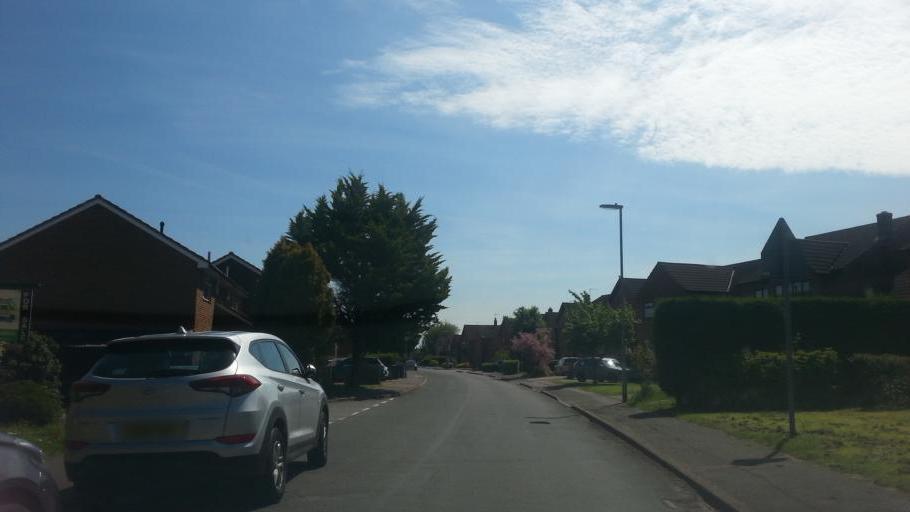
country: GB
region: England
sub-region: Cambridgeshire
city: Warboys
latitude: 52.4061
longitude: -0.0807
